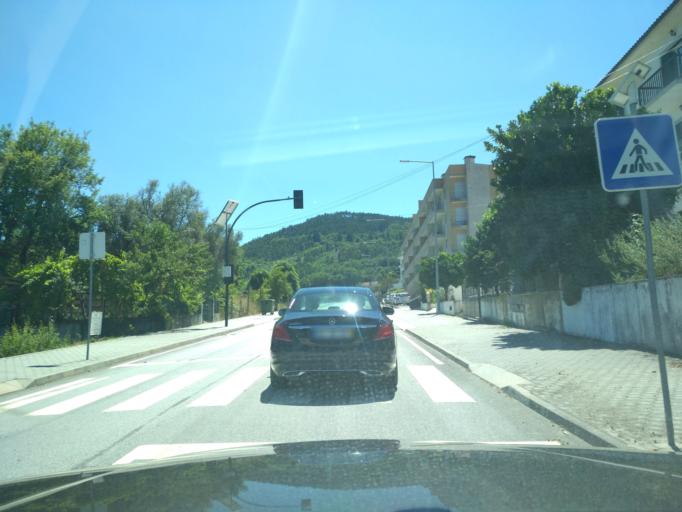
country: PT
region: Vila Real
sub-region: Ribeira de Pena
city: Ribeira de Pena
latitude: 41.5207
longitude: -7.7919
